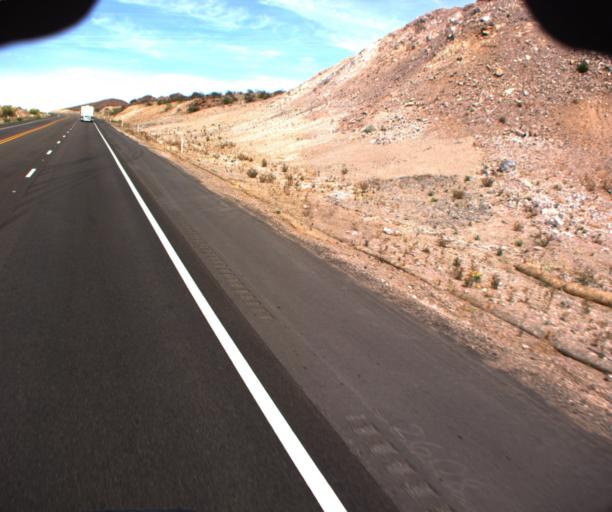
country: US
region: Arizona
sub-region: Mohave County
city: Desert Hills
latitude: 34.6239
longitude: -114.3353
